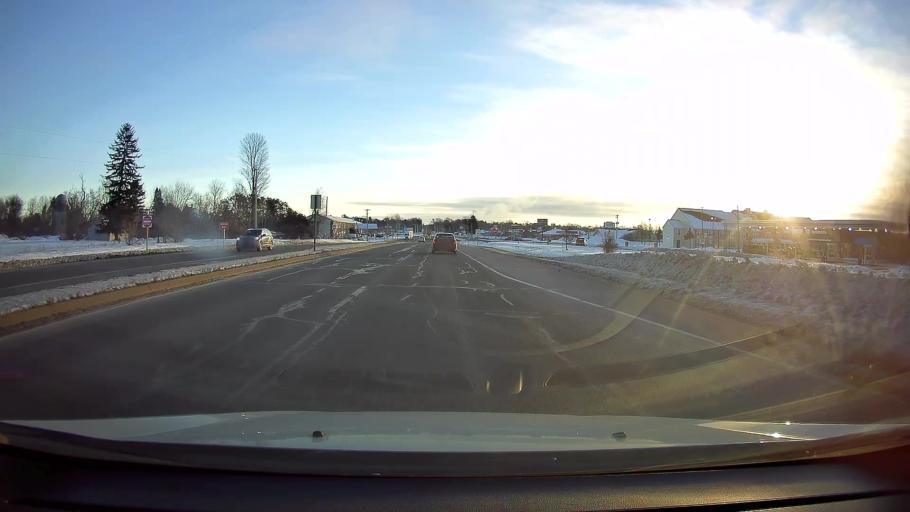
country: US
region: Wisconsin
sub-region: Barron County
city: Turtle Lake
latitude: 45.3953
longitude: -92.1583
